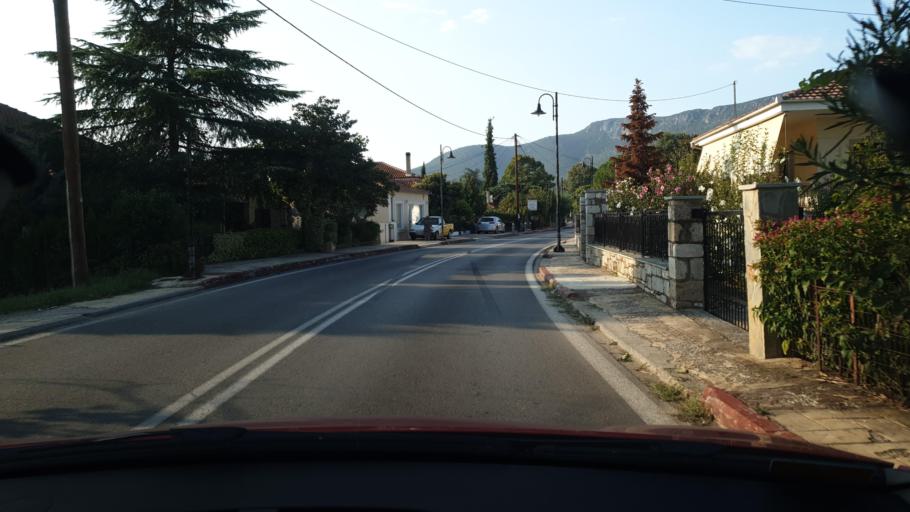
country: GR
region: Thessaly
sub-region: Nomos Magnisias
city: Sourpi
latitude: 39.1019
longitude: 22.8938
